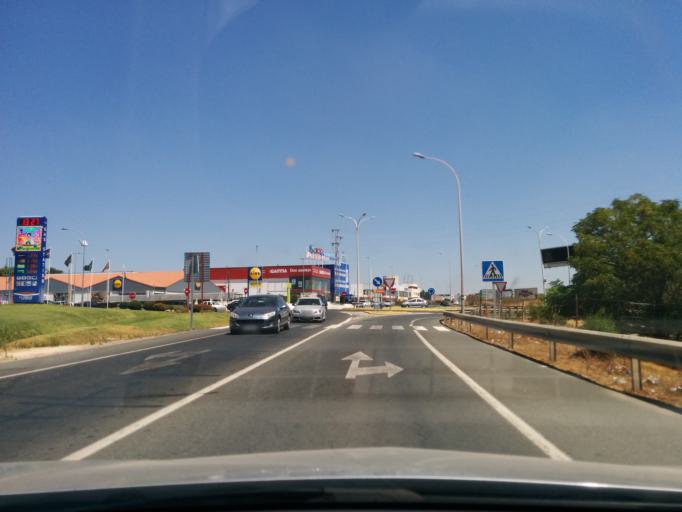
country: ES
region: Andalusia
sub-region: Provincia de Sevilla
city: Benacazon
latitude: 37.3617
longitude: -6.2000
